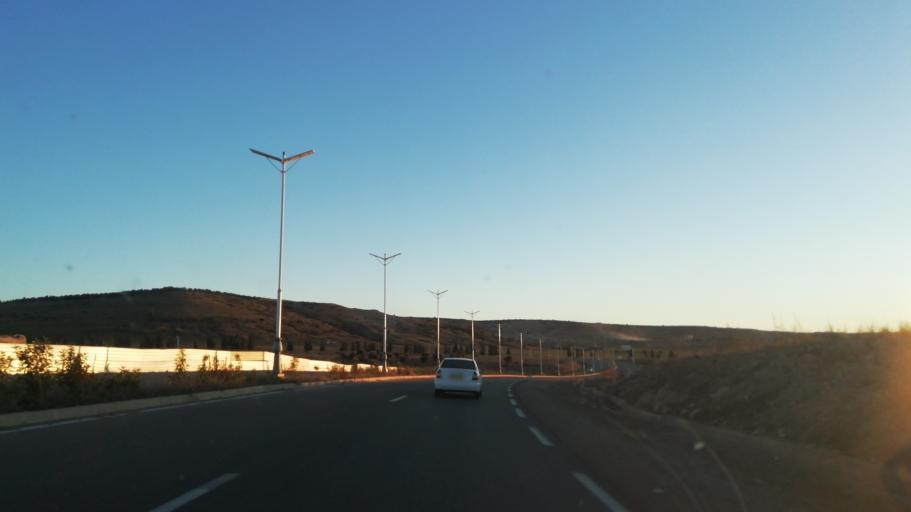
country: DZ
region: Saida
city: Saida
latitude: 34.8571
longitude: 0.1977
